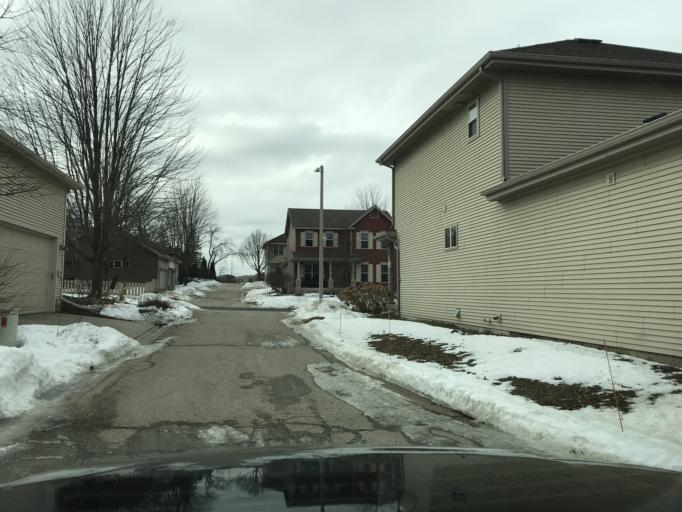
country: US
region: Wisconsin
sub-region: Dane County
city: Monona
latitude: 43.0887
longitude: -89.2790
